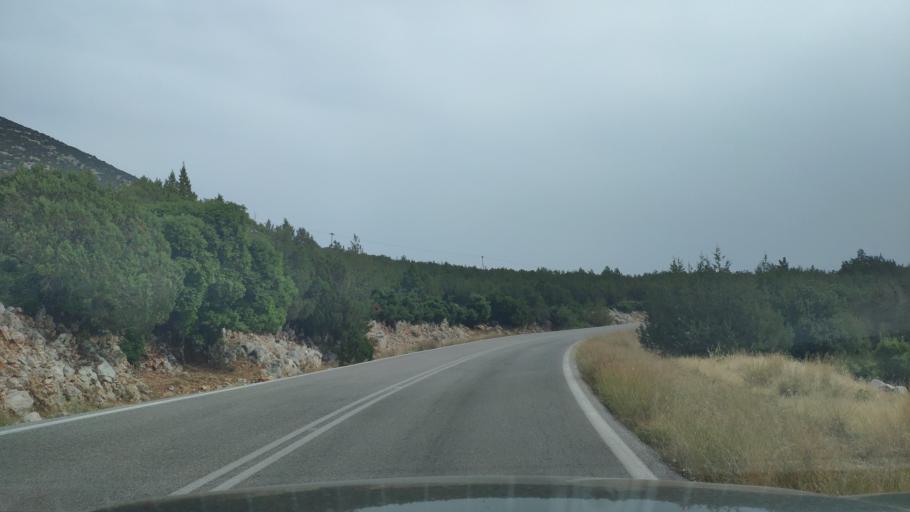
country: GR
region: Peloponnese
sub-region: Nomos Argolidos
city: Didyma
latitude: 37.5034
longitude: 23.1926
